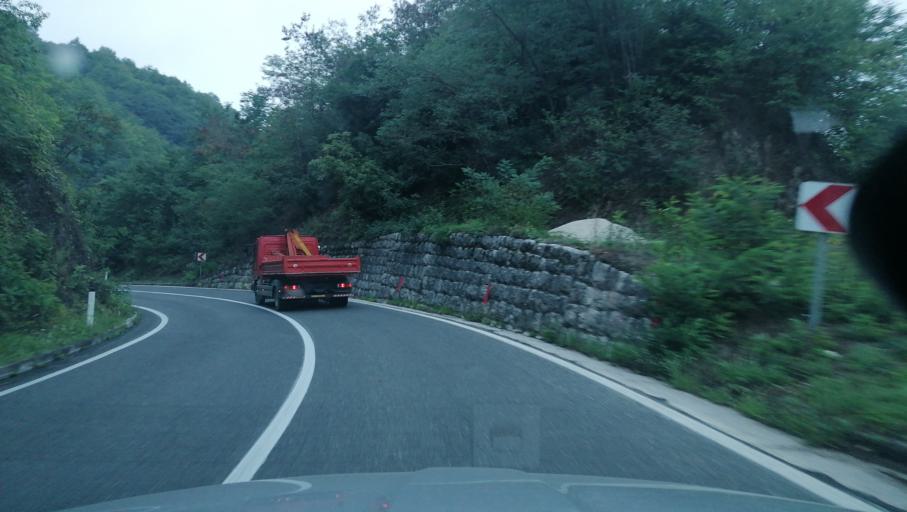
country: BA
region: Federation of Bosnia and Herzegovina
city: Jablanica
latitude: 43.7203
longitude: 17.7090
